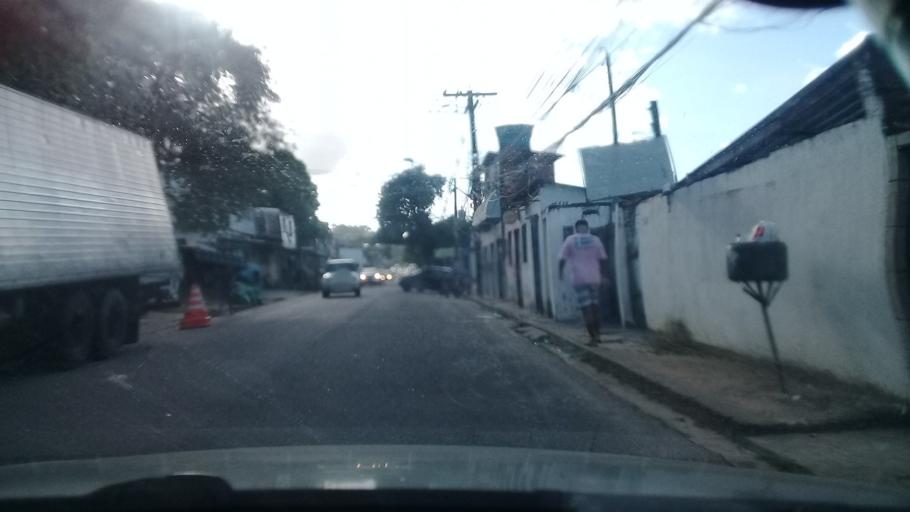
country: BR
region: Pernambuco
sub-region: Jaboatao Dos Guararapes
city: Jaboatao dos Guararapes
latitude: -8.1200
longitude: -34.9387
